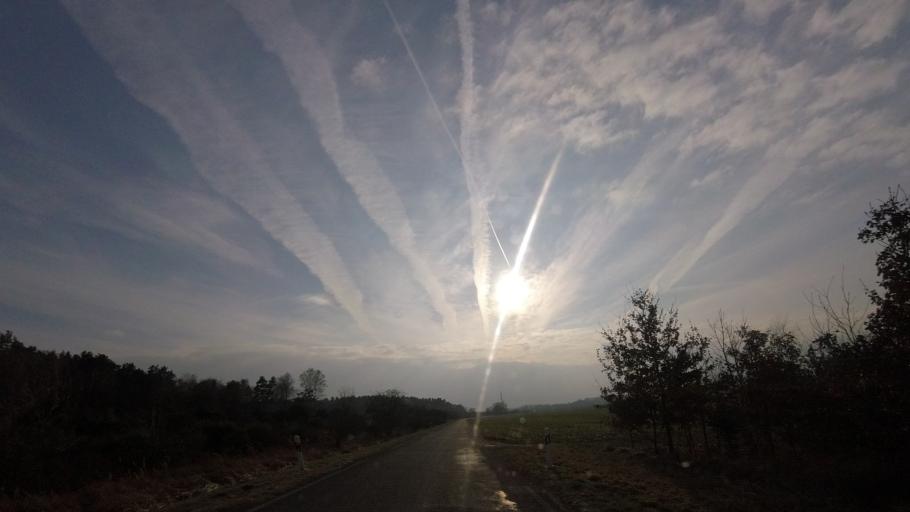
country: DE
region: Brandenburg
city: Belzig
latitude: 52.1237
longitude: 12.5592
